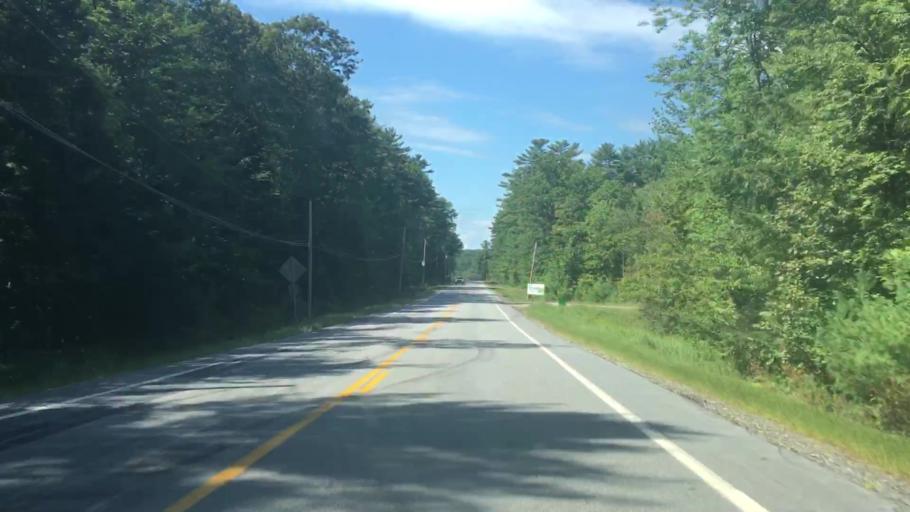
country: US
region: Maine
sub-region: Kennebec County
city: Monmouth
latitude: 44.1848
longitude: -69.9551
